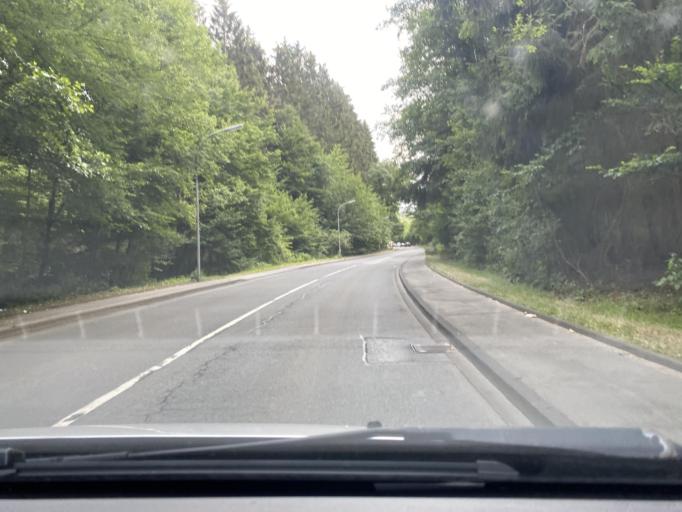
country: DE
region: North Rhine-Westphalia
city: Werdohl
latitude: 51.2585
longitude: 7.7813
